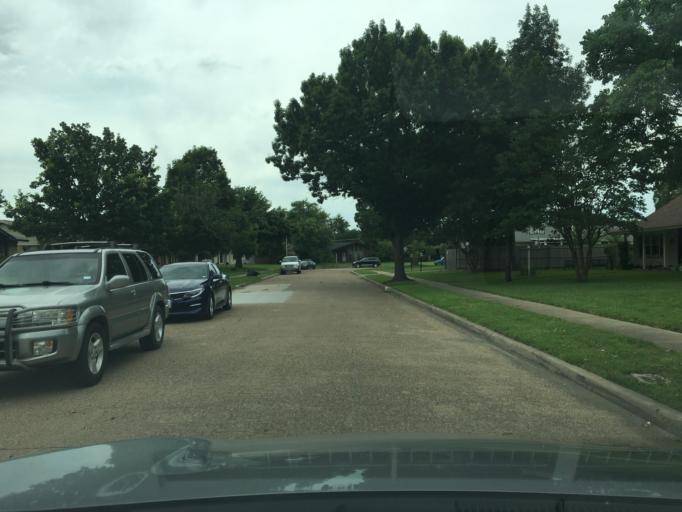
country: US
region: Texas
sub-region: Dallas County
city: Richardson
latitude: 32.9327
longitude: -96.7033
